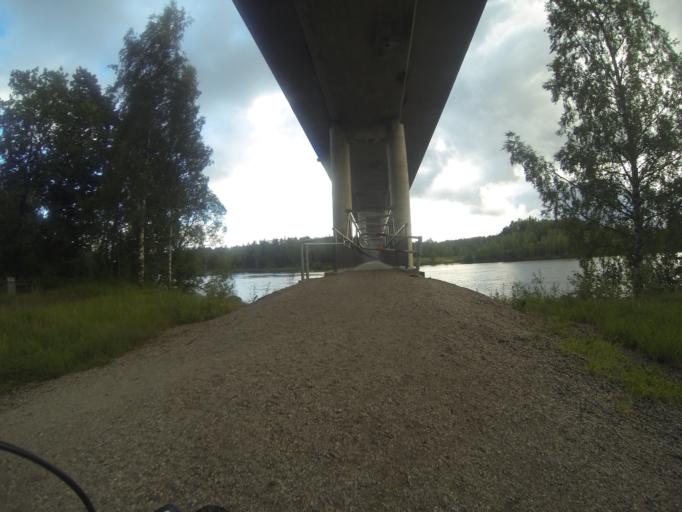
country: SE
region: Dalarna
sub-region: Avesta Kommun
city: Avesta
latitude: 60.1487
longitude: 16.2002
